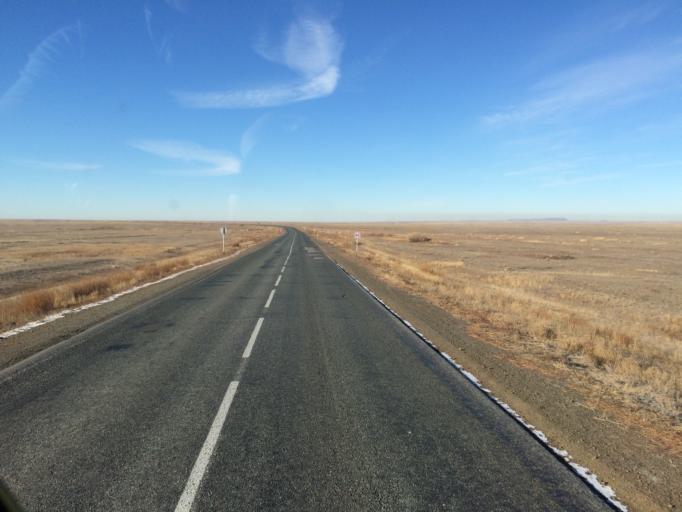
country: KZ
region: Aqtoebe
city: Khromtau
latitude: 50.1857
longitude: 58.6762
